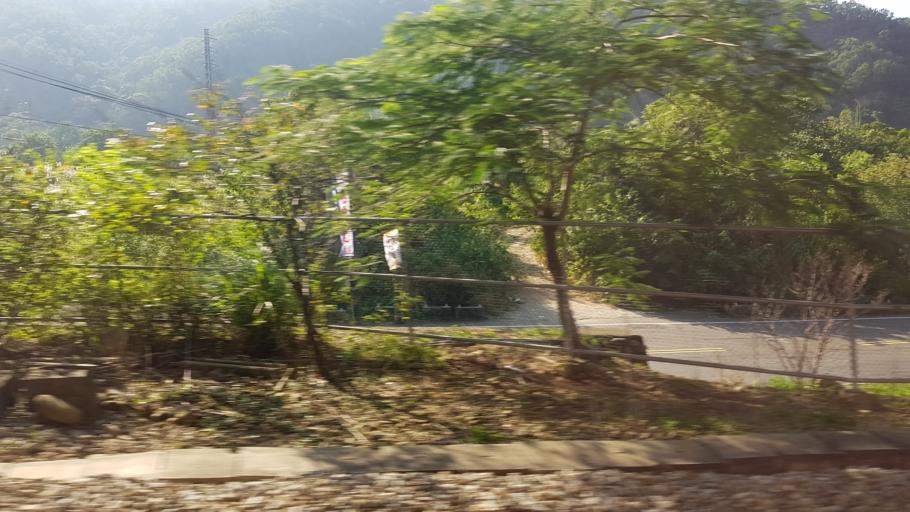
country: TW
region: Taiwan
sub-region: Miaoli
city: Miaoli
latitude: 24.4244
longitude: 120.7742
